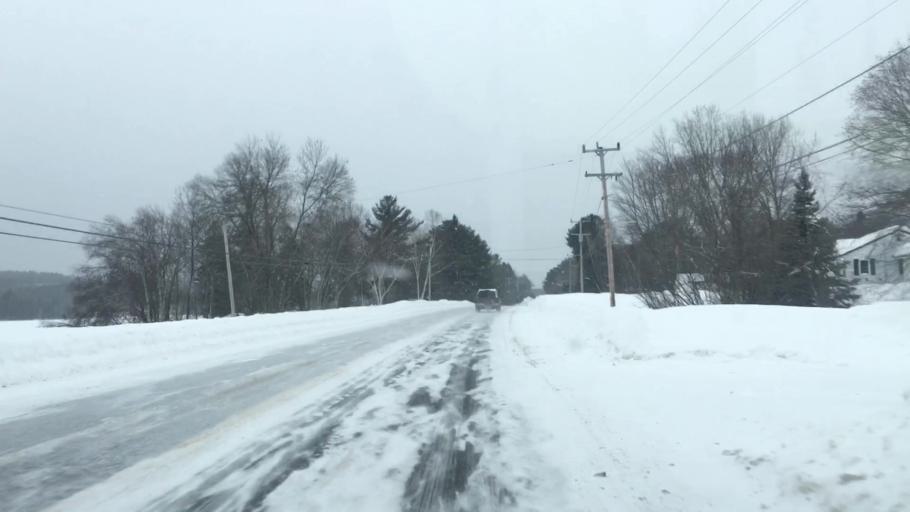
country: US
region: Maine
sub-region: Penobscot County
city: Medway
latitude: 45.5954
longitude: -68.4918
